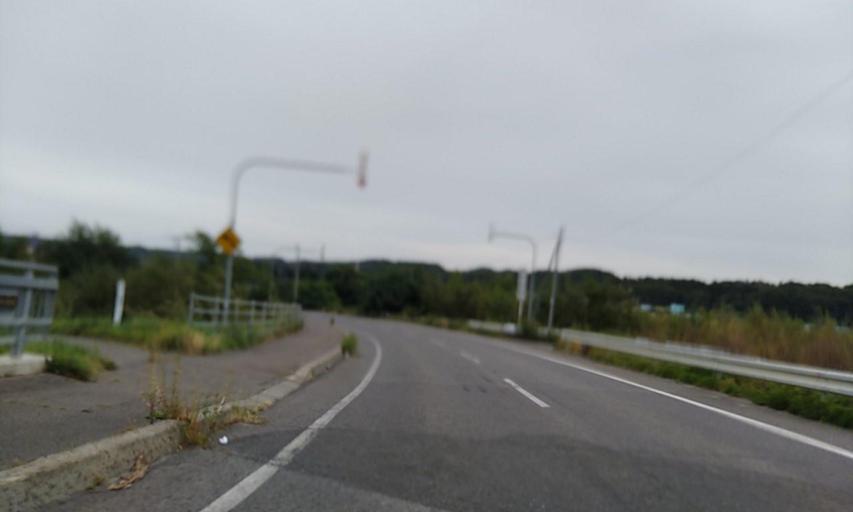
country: JP
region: Hokkaido
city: Bihoro
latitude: 43.8392
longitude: 144.1145
